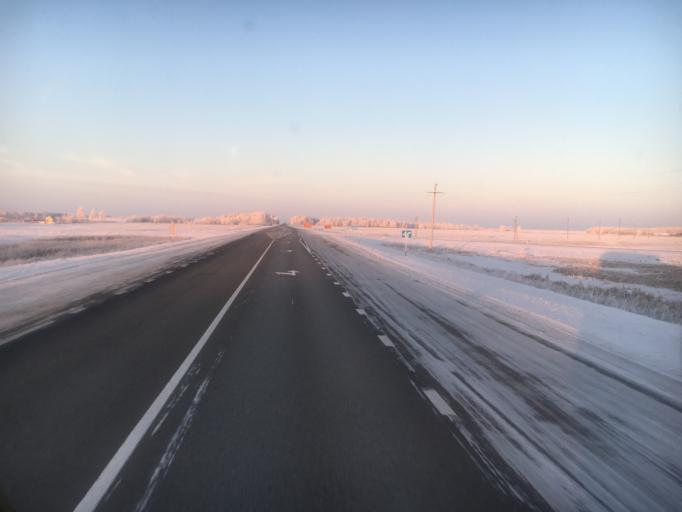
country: KZ
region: Soltustik Qazaqstan
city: Smirnovo
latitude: 54.3444
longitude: 69.1589
